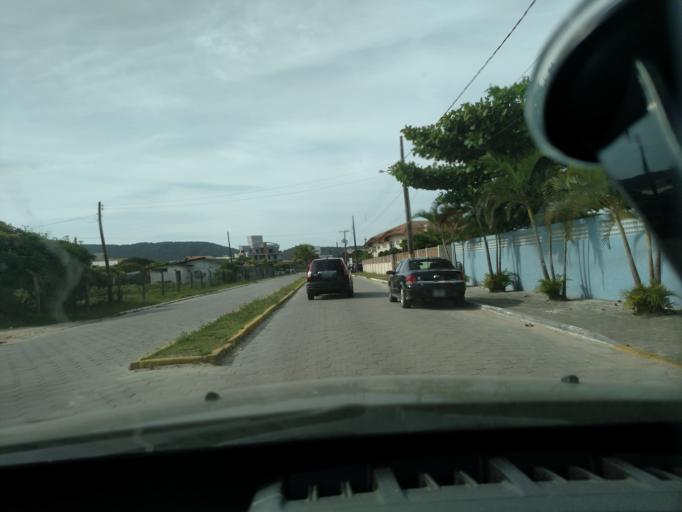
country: BR
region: Santa Catarina
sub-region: Porto Belo
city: Porto Belo
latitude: -27.1883
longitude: -48.4998
